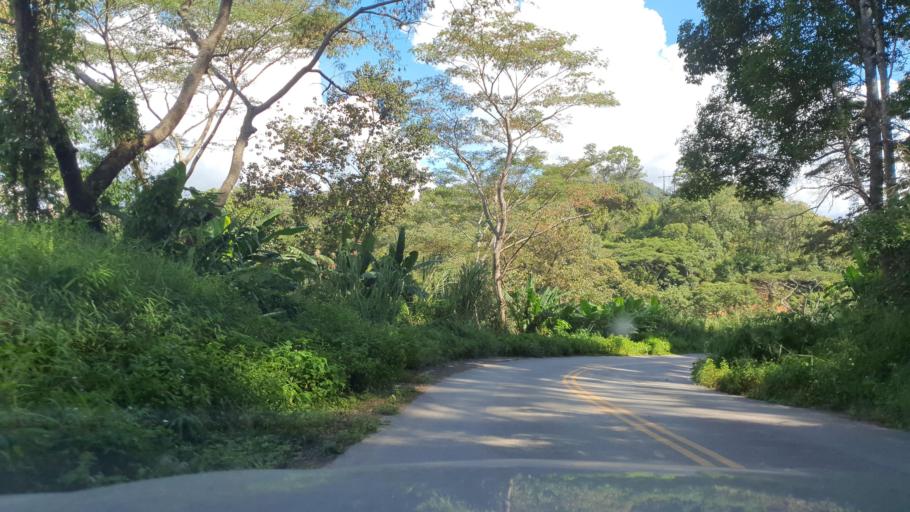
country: TH
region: Chiang Mai
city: Phrao
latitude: 19.3071
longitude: 99.3429
